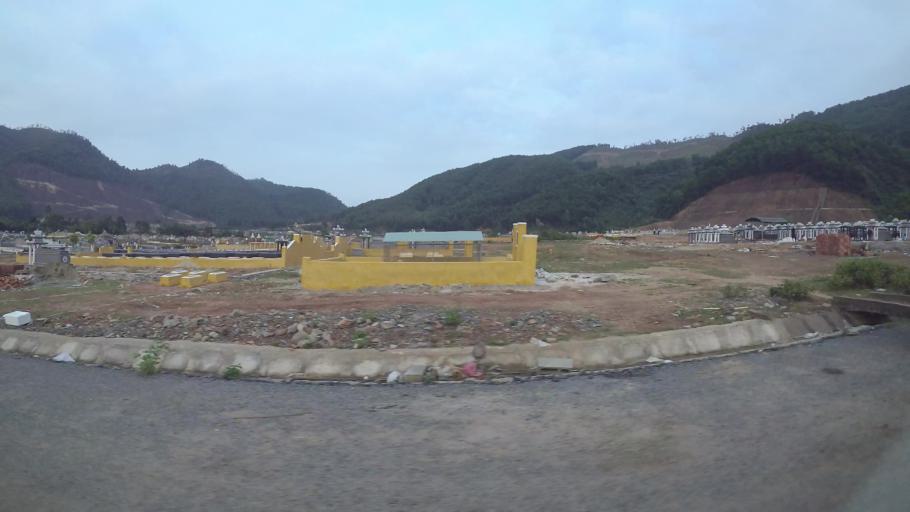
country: VN
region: Da Nang
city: Lien Chieu
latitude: 16.0554
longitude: 108.1233
